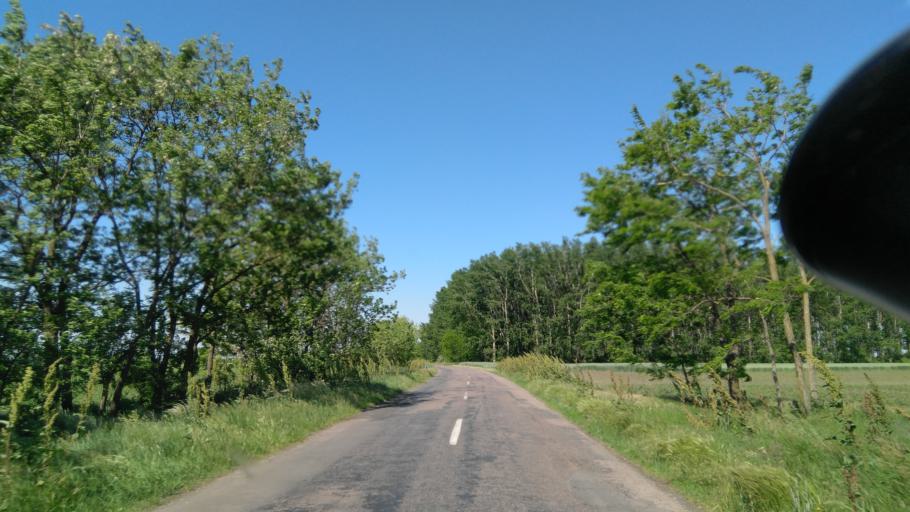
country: HU
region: Bekes
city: Kunagota
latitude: 46.4256
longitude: 21.0876
